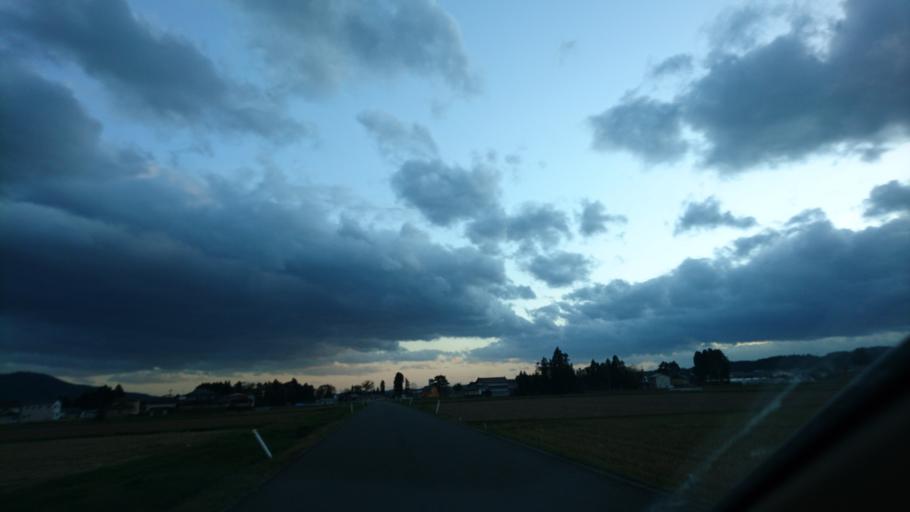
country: JP
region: Iwate
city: Mizusawa
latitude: 39.0675
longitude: 141.1413
